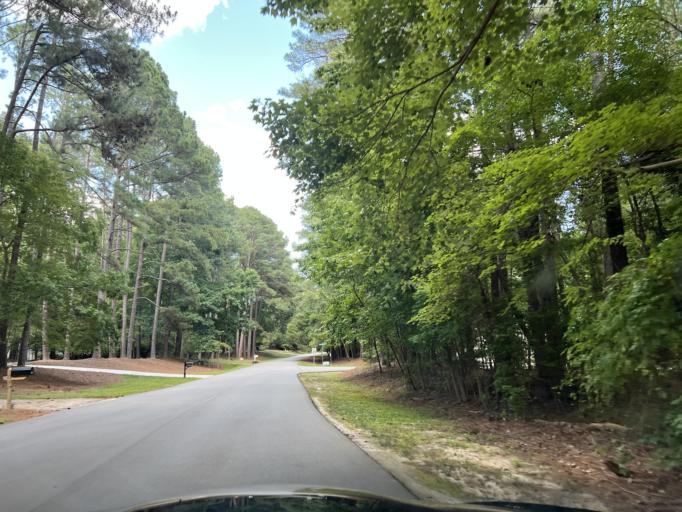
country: US
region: North Carolina
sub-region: Wake County
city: Wake Forest
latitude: 35.9388
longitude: -78.6438
